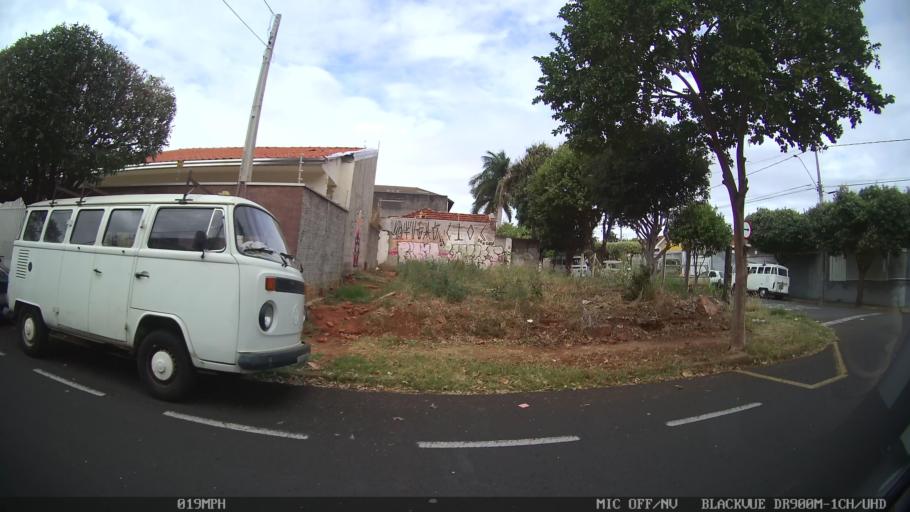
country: BR
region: Sao Paulo
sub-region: Sao Jose Do Rio Preto
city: Sao Jose do Rio Preto
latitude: -20.8153
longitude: -49.3711
